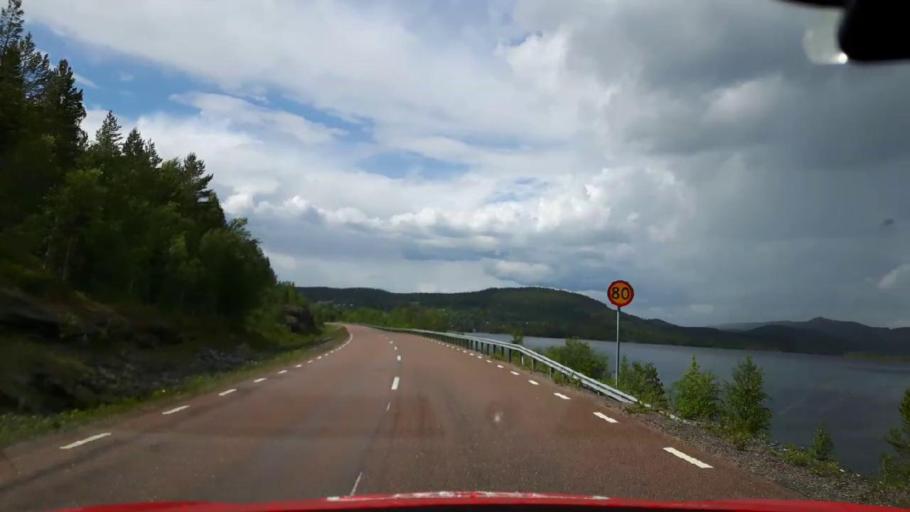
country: SE
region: Jaemtland
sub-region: Krokoms Kommun
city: Valla
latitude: 63.8987
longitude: 14.2455
